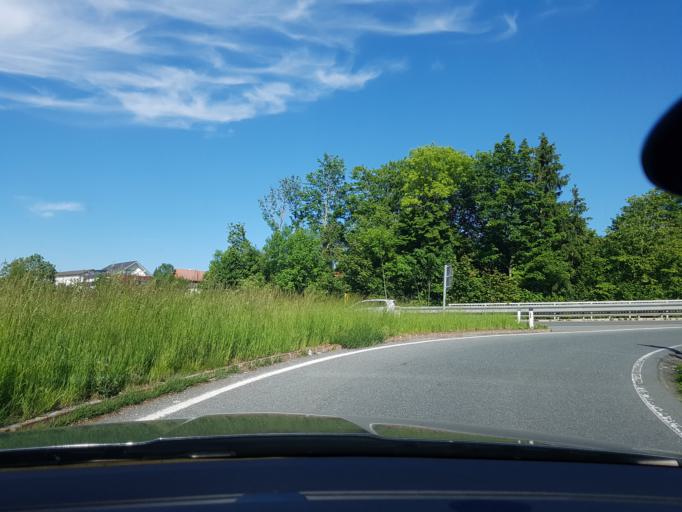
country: AT
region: Salzburg
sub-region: Politischer Bezirk Salzburg-Umgebung
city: Mattsee
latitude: 47.9642
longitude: 13.0967
